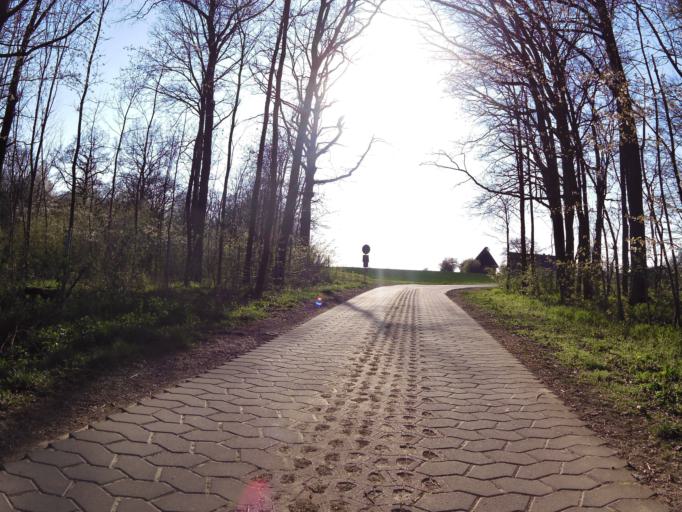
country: DE
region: Bavaria
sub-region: Regierungsbezirk Unterfranken
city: Rottendorf
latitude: 49.8232
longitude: 10.0658
